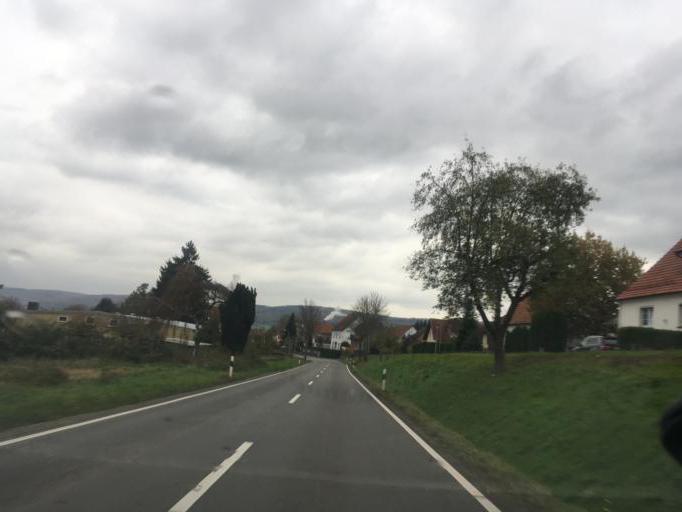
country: DE
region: Lower Saxony
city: Bodenfelde
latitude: 51.6193
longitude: 9.5531
